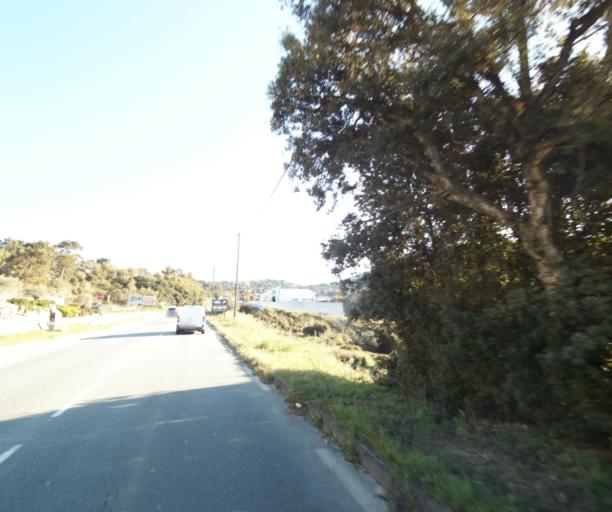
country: FR
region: Corsica
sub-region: Departement de la Corse-du-Sud
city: Propriano
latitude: 41.6636
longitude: 8.9186
